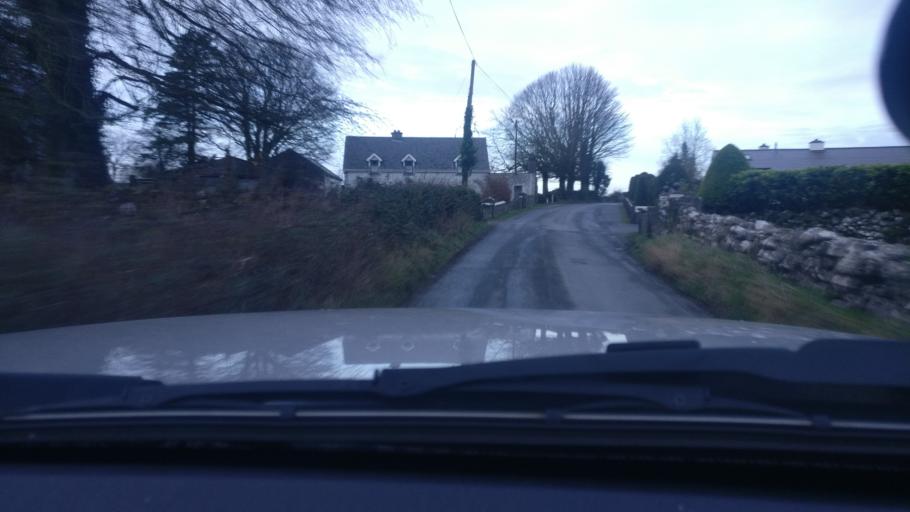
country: IE
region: Connaught
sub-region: County Galway
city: Loughrea
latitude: 53.1880
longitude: -8.5134
